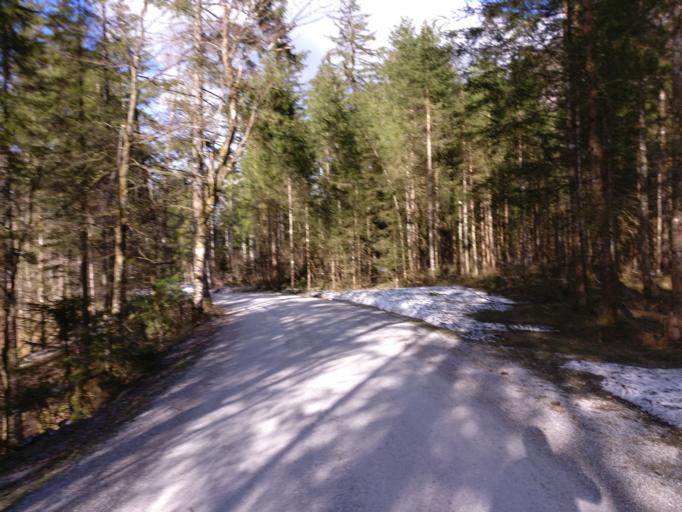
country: AT
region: Salzburg
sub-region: Politischer Bezirk Hallein
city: Golling an der Salzach
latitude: 47.5776
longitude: 13.1427
